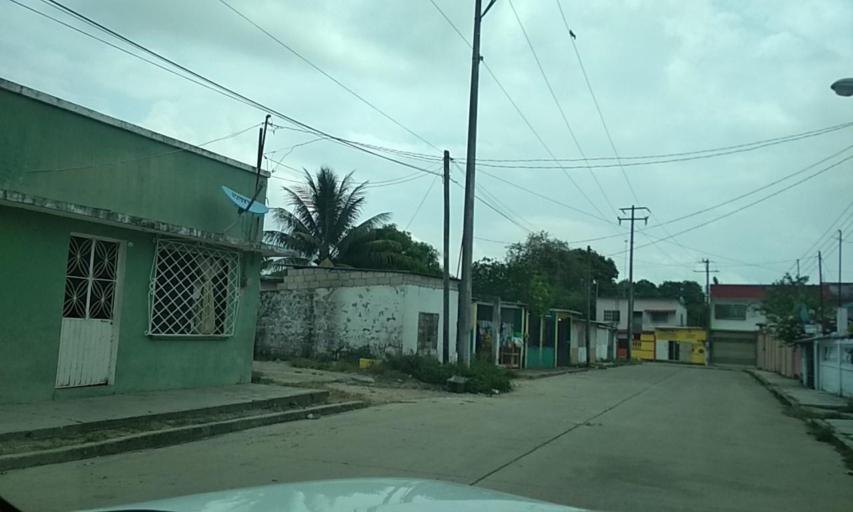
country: MX
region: Veracruz
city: Las Choapas
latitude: 17.8975
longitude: -94.0988
